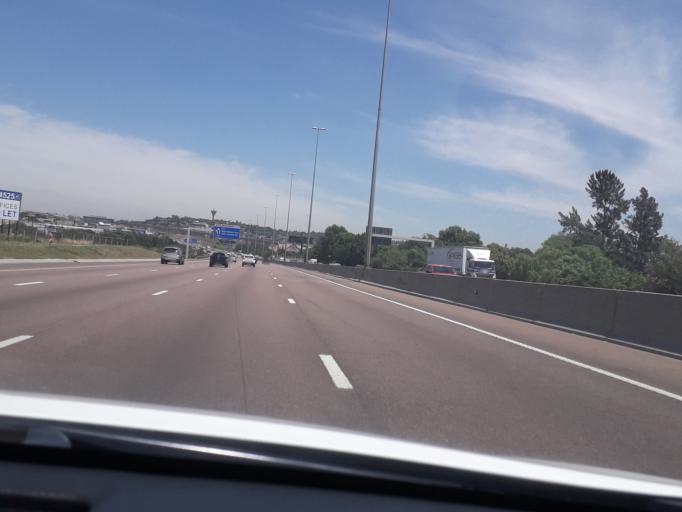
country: ZA
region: Gauteng
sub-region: City of Tshwane Metropolitan Municipality
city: Centurion
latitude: -25.8621
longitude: 28.2072
